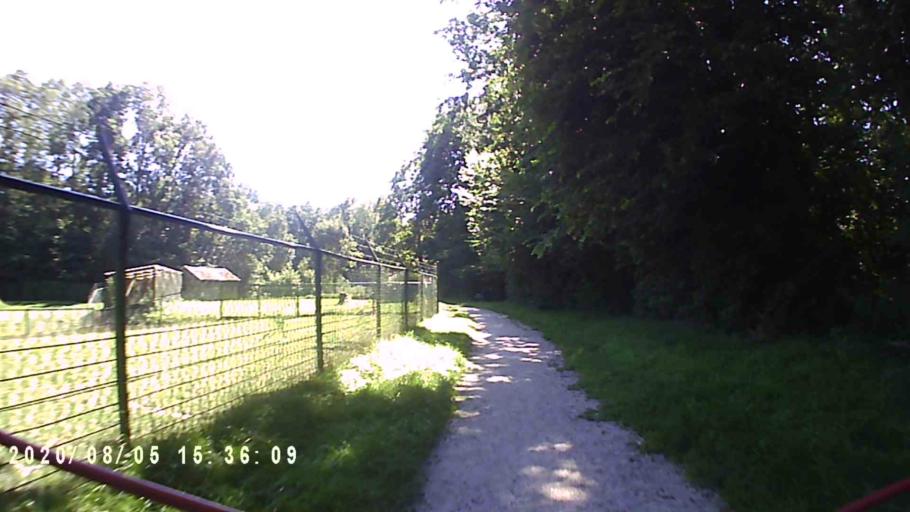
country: NL
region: Groningen
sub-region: Gemeente Winsum
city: Winsum
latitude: 53.3625
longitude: 6.4672
